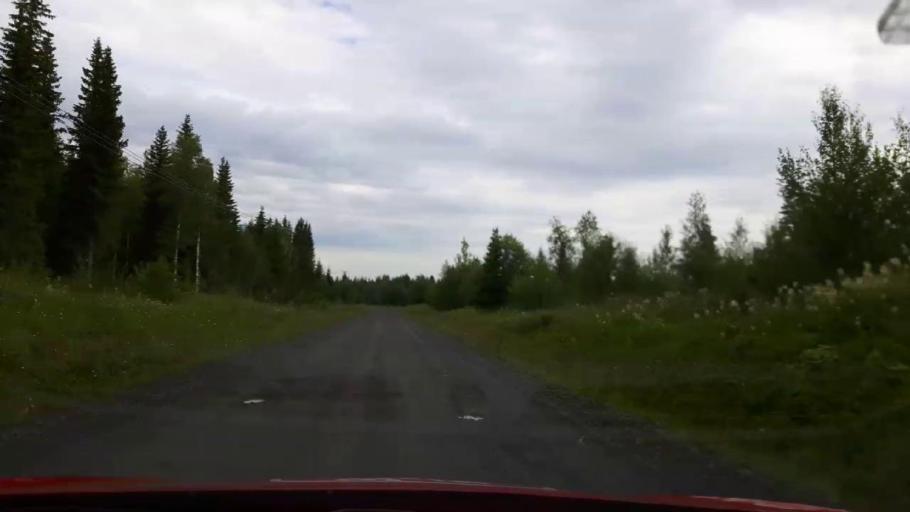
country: SE
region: Jaemtland
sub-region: Stroemsunds Kommun
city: Stroemsund
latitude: 63.4927
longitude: 15.3140
